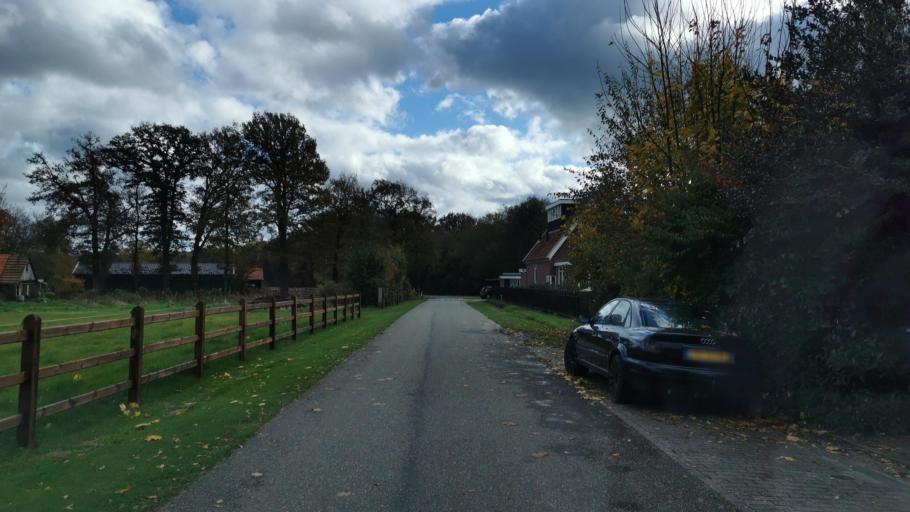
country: NL
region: Overijssel
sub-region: Gemeente Enschede
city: Enschede
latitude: 52.1975
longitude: 6.9332
